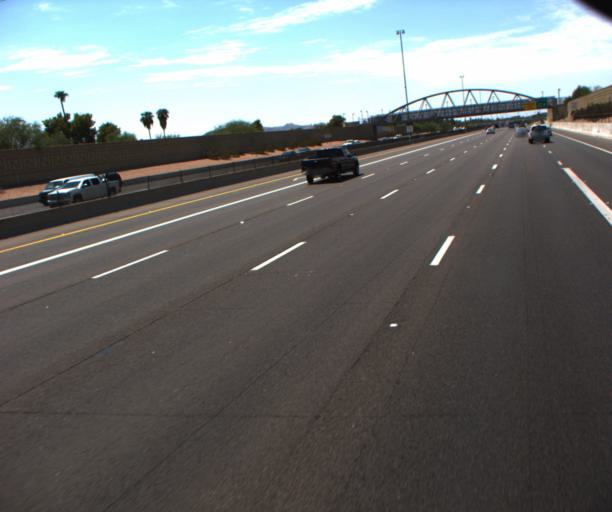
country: US
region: Arizona
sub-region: Maricopa County
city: Tempe Junction
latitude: 33.3858
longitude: -111.9318
